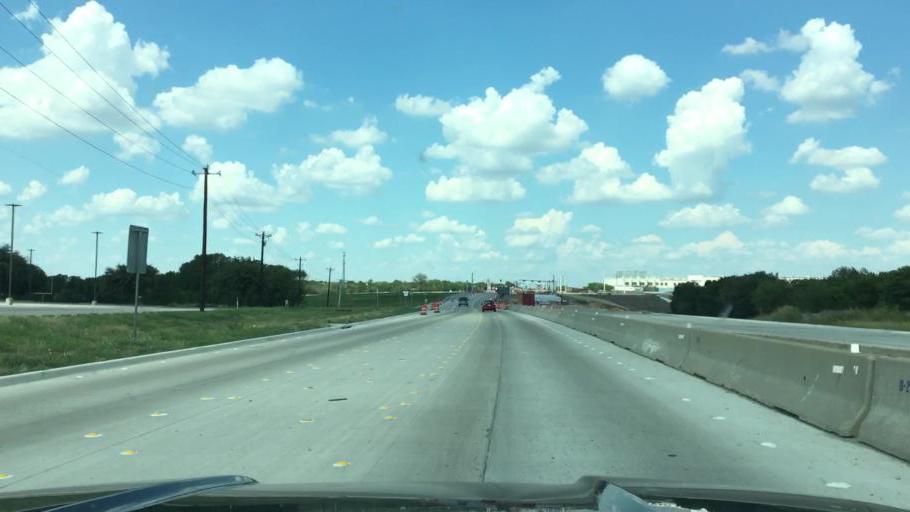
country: US
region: Texas
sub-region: Tarrant County
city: Haslet
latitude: 33.0246
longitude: -97.3108
